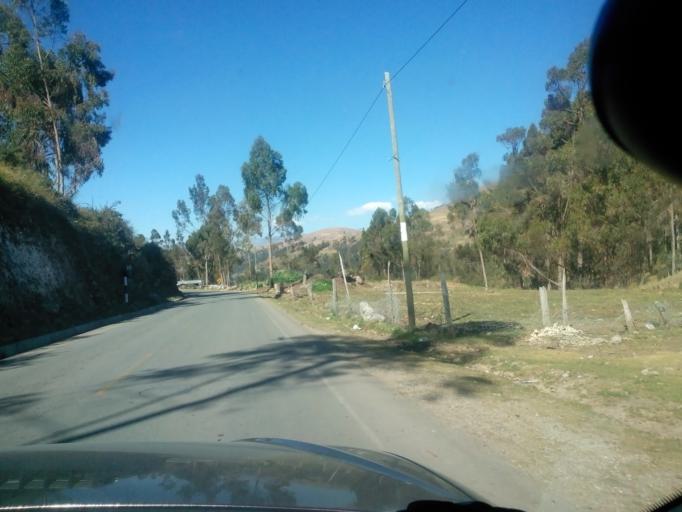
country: PE
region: Apurimac
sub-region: Provincia de Andahuaylas
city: Talavera
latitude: -13.6518
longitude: -73.5271
